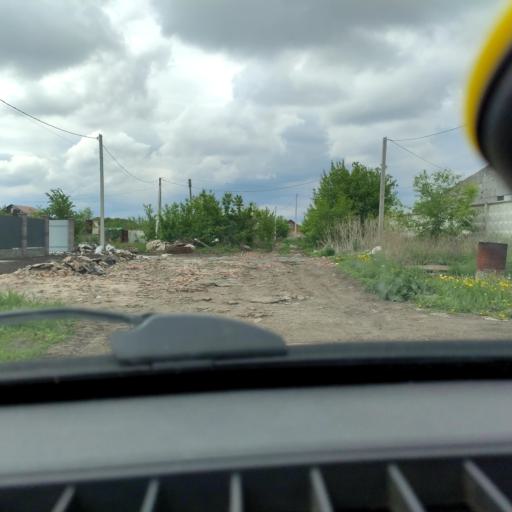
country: RU
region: Samara
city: Tol'yatti
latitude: 53.5713
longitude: 49.4041
